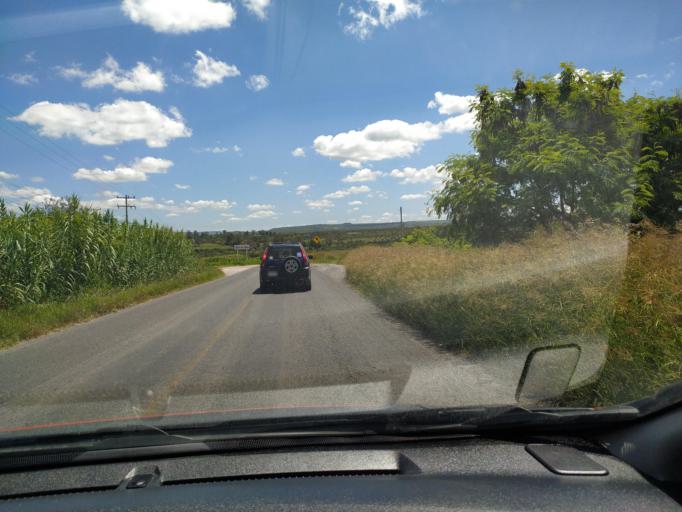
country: MX
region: Jalisco
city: San Julian
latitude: 21.0007
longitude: -102.0989
